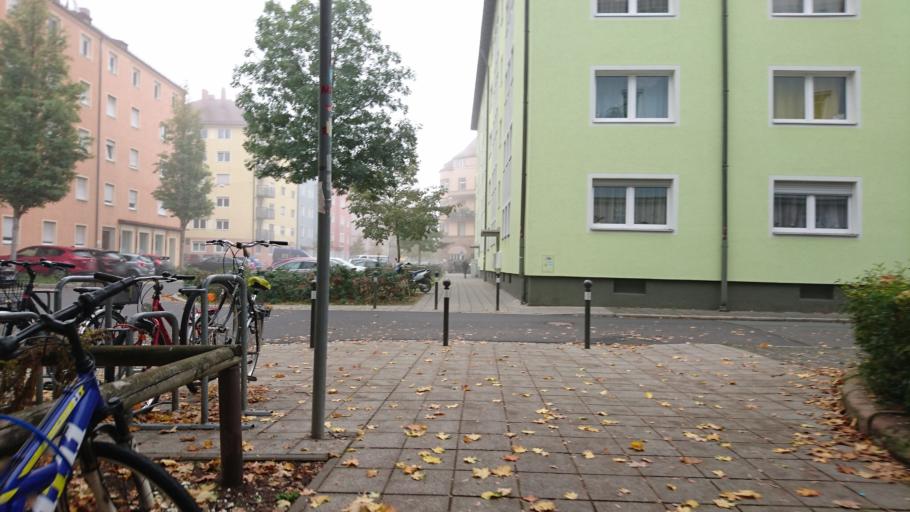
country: DE
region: Bavaria
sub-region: Regierungsbezirk Mittelfranken
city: Nuernberg
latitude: 49.4403
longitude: 11.0994
